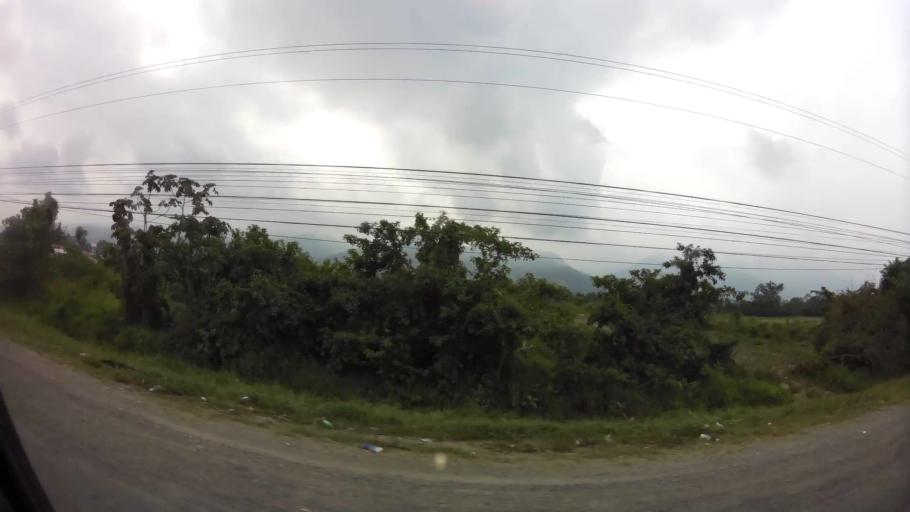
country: HN
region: Yoro
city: El Progreso
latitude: 15.4427
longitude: -87.7914
